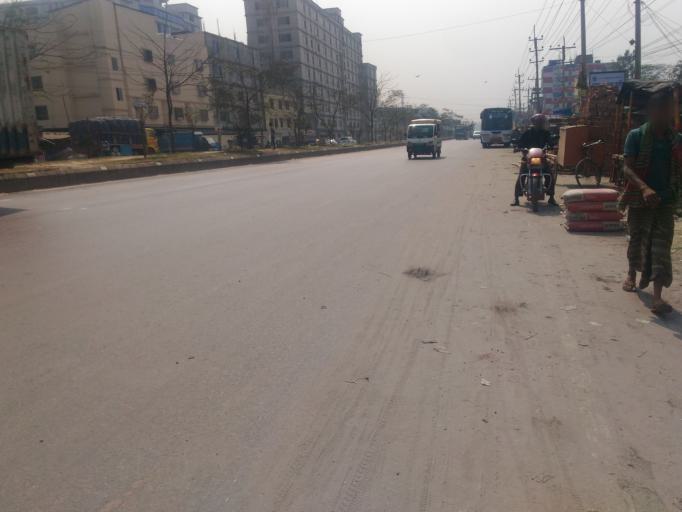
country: BD
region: Dhaka
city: Tungi
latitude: 24.0020
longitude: 90.3828
